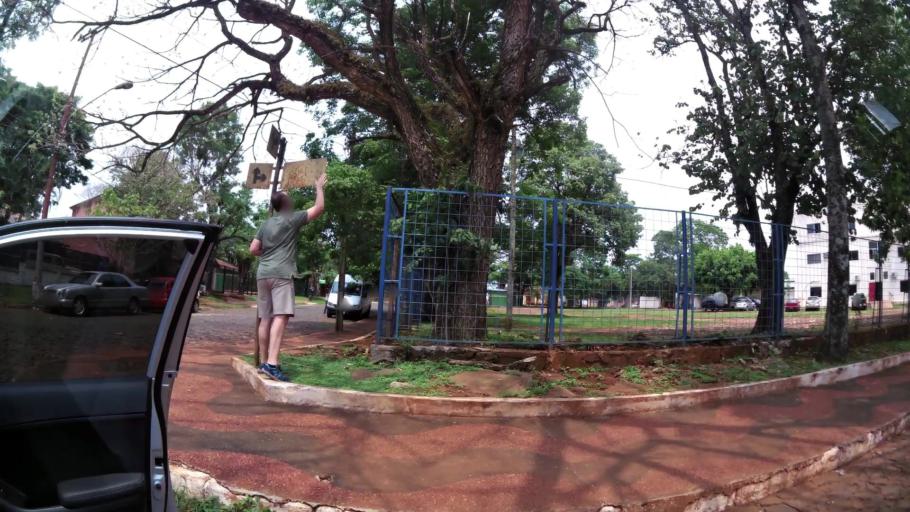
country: PY
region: Alto Parana
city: Presidente Franco
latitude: -25.5512
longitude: -54.6152
